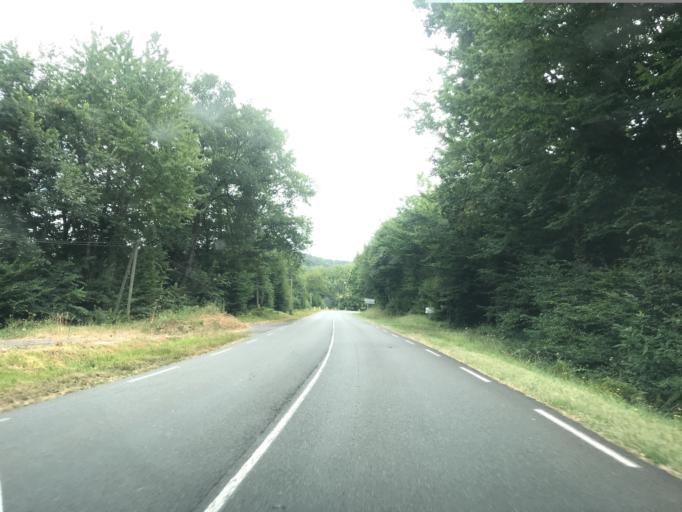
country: FR
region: Aquitaine
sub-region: Departement de la Dordogne
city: Brantome
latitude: 45.4073
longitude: 0.5807
